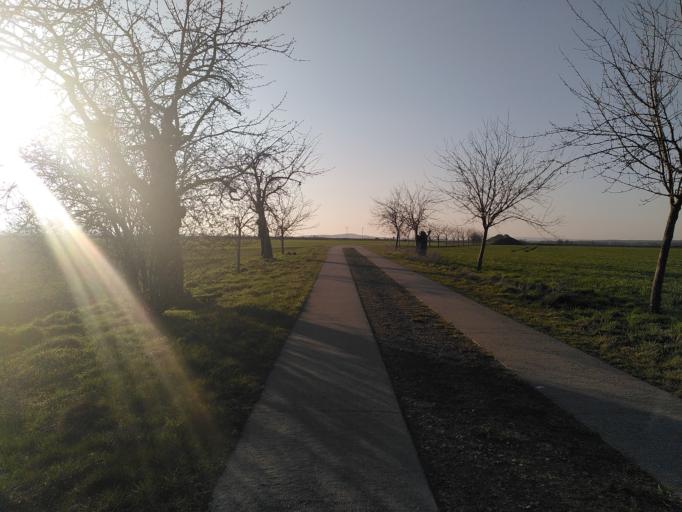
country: DE
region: Saxony-Anhalt
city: Gatersleben
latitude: 51.7994
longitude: 11.2541
